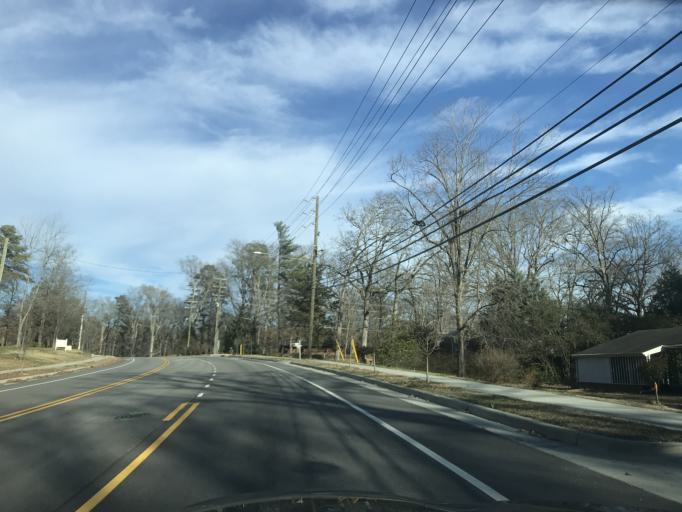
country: US
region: North Carolina
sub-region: Wake County
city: Cary
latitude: 35.7747
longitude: -78.7338
